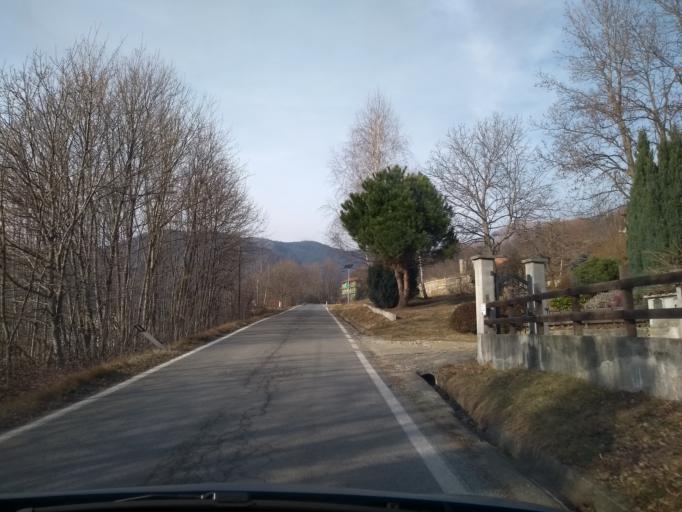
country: IT
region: Piedmont
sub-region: Provincia di Torino
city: Coassolo
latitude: 45.3025
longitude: 7.4808
